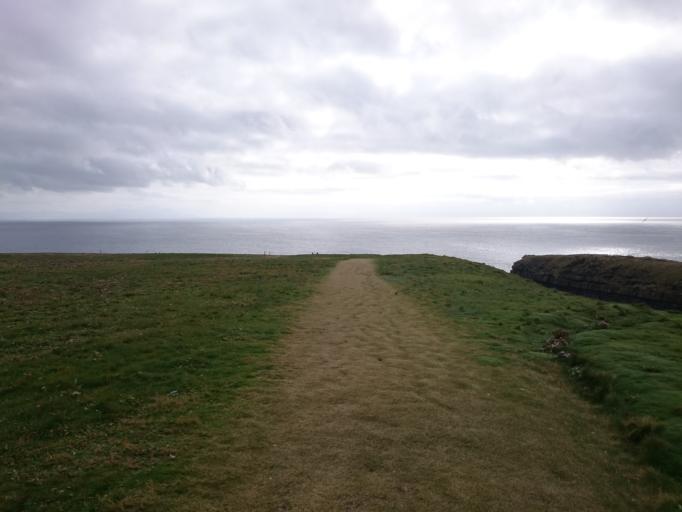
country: IE
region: Munster
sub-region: Ciarrai
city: Ballybunnion
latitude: 52.5607
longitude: -9.9361
